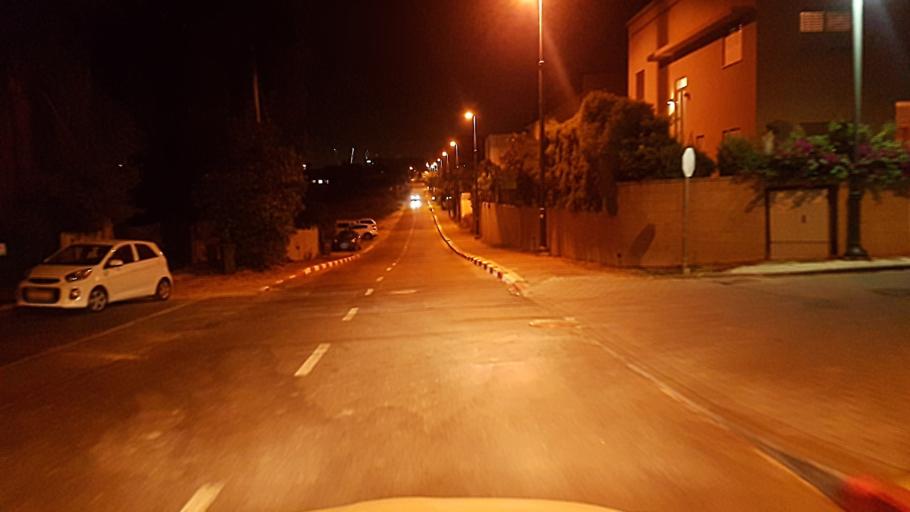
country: IL
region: Central District
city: Hod HaSharon
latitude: 32.1637
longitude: 34.8899
